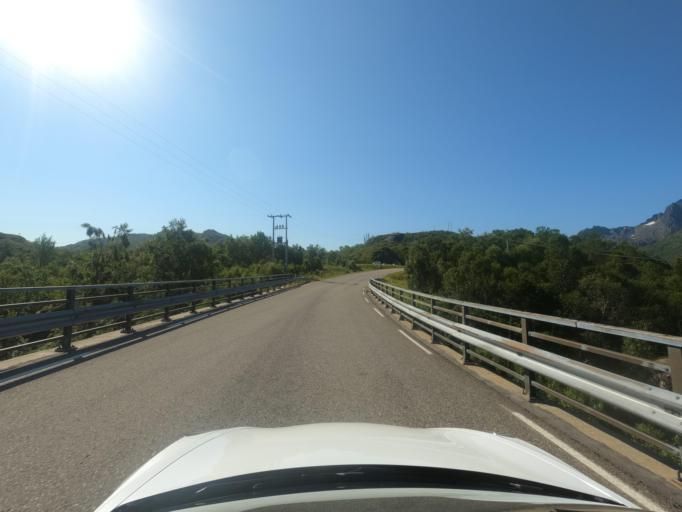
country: NO
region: Nordland
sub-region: Hadsel
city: Stokmarknes
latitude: 68.4362
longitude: 15.1826
